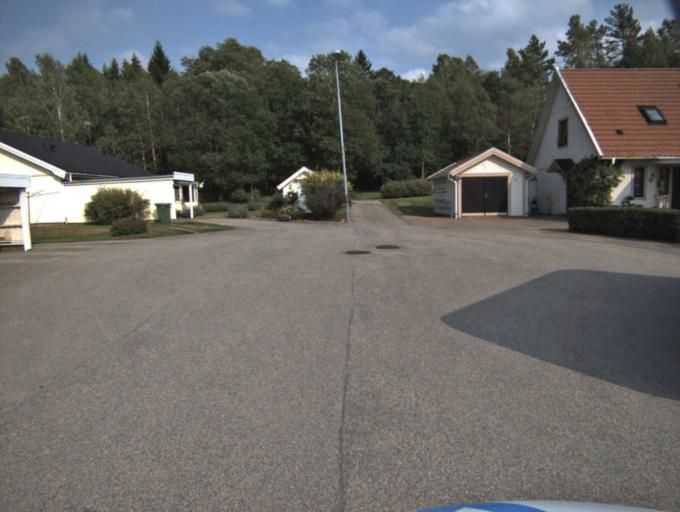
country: SE
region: Vaestra Goetaland
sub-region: Ulricehamns Kommun
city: Ulricehamn
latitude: 57.7811
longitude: 13.4293
